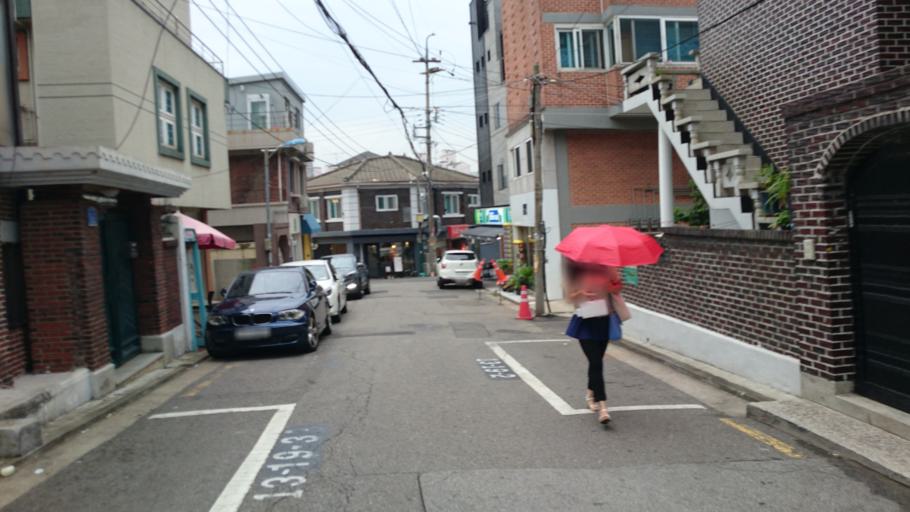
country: KR
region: Seoul
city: Seoul
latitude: 37.5657
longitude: 126.9237
